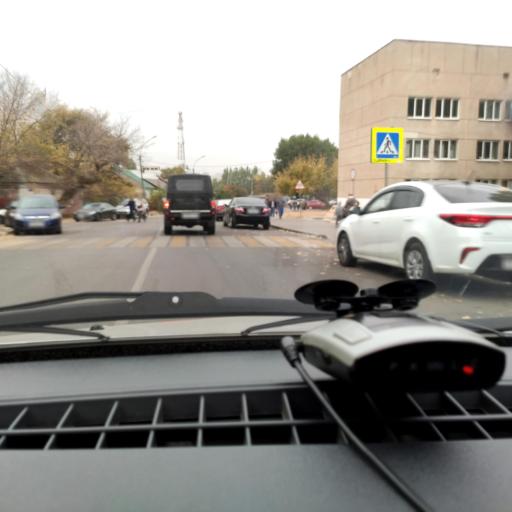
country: RU
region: Voronezj
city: Voronezh
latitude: 51.6563
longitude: 39.2421
